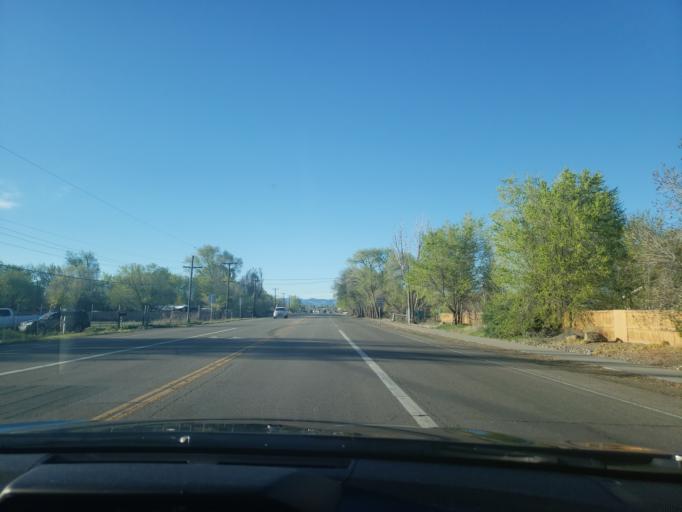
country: US
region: Colorado
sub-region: Mesa County
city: Fruita
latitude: 39.1462
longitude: -108.7382
